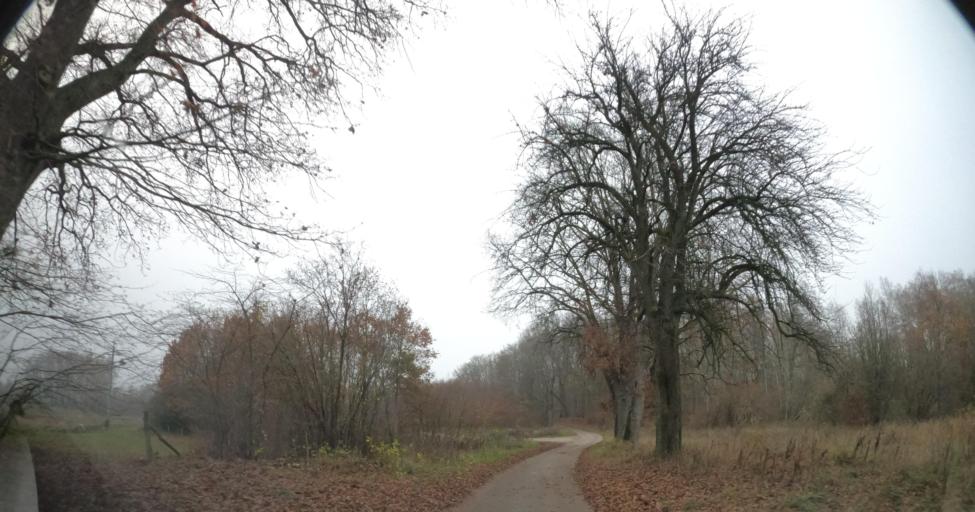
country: PL
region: West Pomeranian Voivodeship
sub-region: Powiat drawski
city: Drawsko Pomorskie
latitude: 53.5804
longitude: 15.8064
